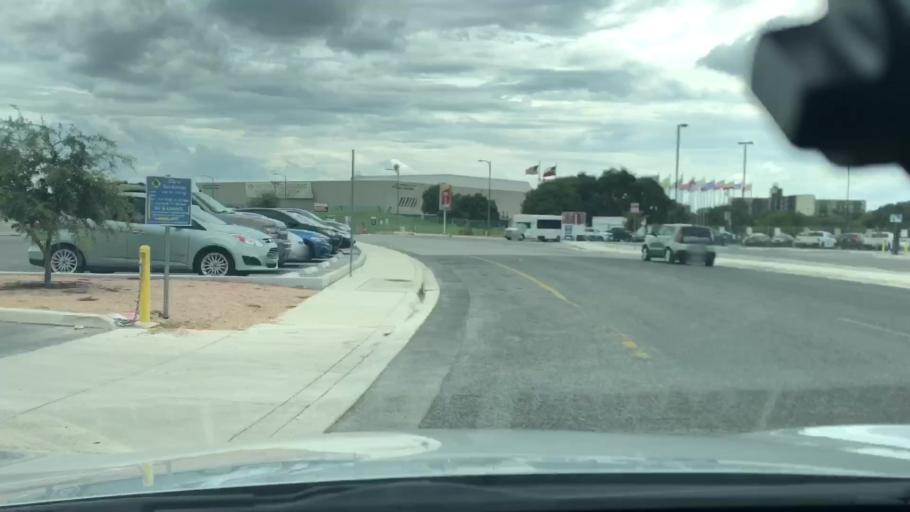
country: US
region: Texas
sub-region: Bexar County
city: San Antonio
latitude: 29.4190
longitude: -98.4820
